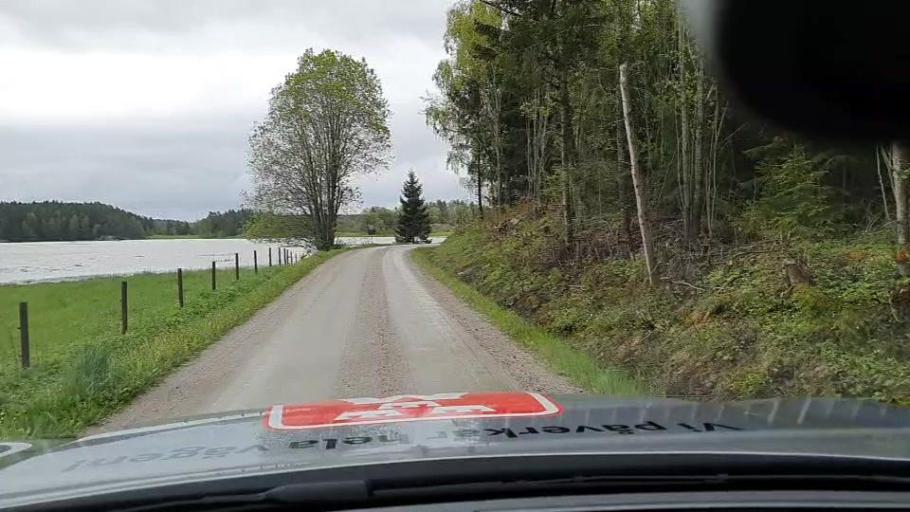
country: SE
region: Soedermanland
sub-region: Nykopings Kommun
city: Svalsta
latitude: 58.6441
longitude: 16.9333
